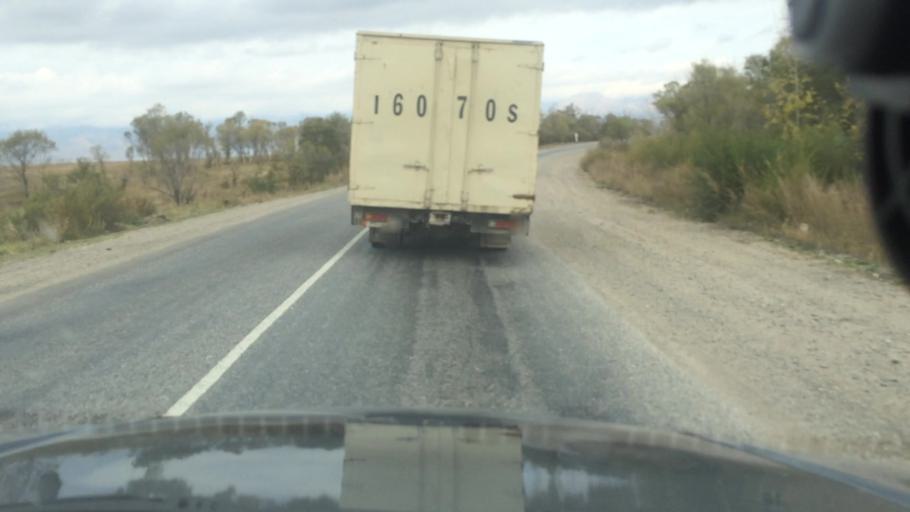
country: KG
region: Ysyk-Koel
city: Tyup
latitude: 42.6676
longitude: 78.3489
